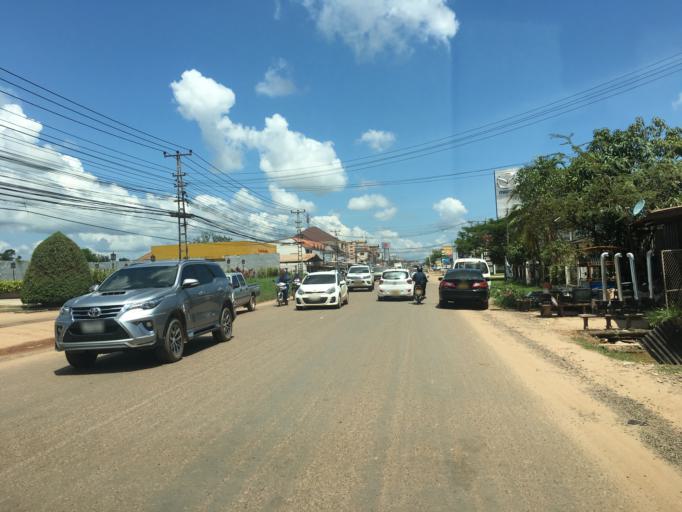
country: TH
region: Nong Khai
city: Si Chiang Mai
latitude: 17.9807
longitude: 102.5544
